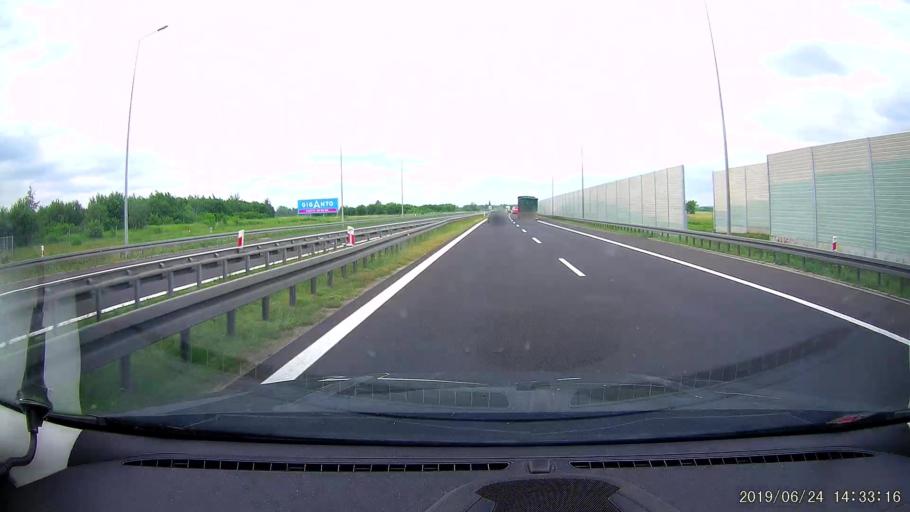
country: PL
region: Lesser Poland Voivodeship
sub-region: Powiat tarnowski
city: Wierzchoslawice
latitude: 50.0456
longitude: 20.8956
